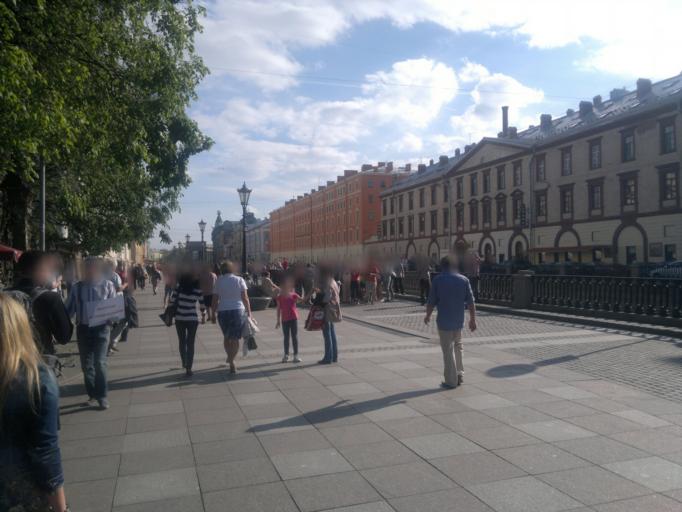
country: RU
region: St.-Petersburg
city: Saint Petersburg
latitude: 59.9394
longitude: 30.3283
